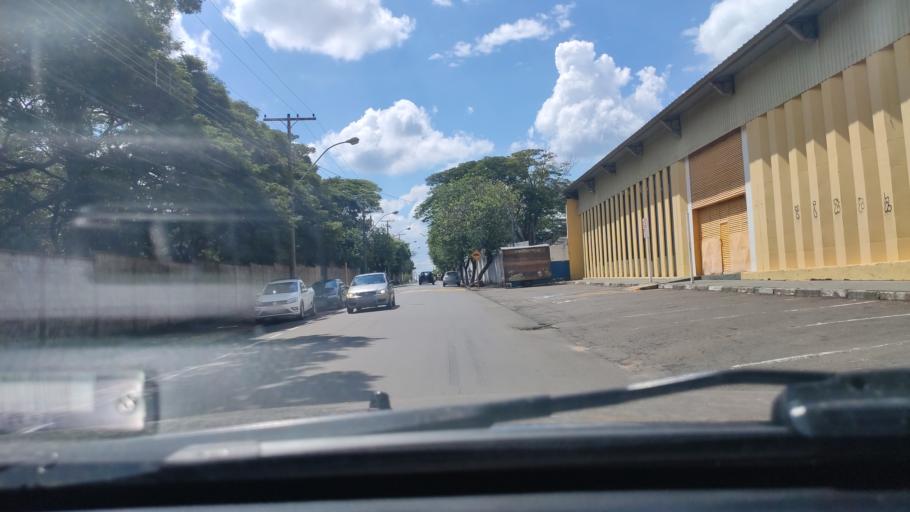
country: BR
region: Sao Paulo
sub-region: Sao Carlos
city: Sao Carlos
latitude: -22.0017
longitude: -47.8798
